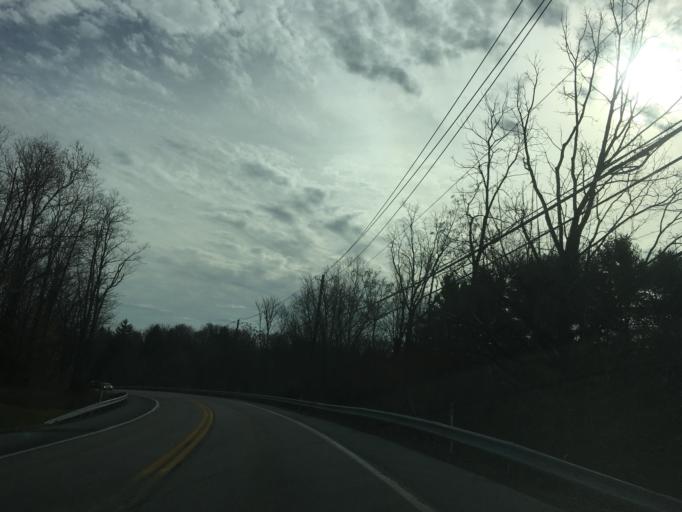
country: US
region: Pennsylvania
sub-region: Dauphin County
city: Colonial Park
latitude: 40.3235
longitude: -76.8264
